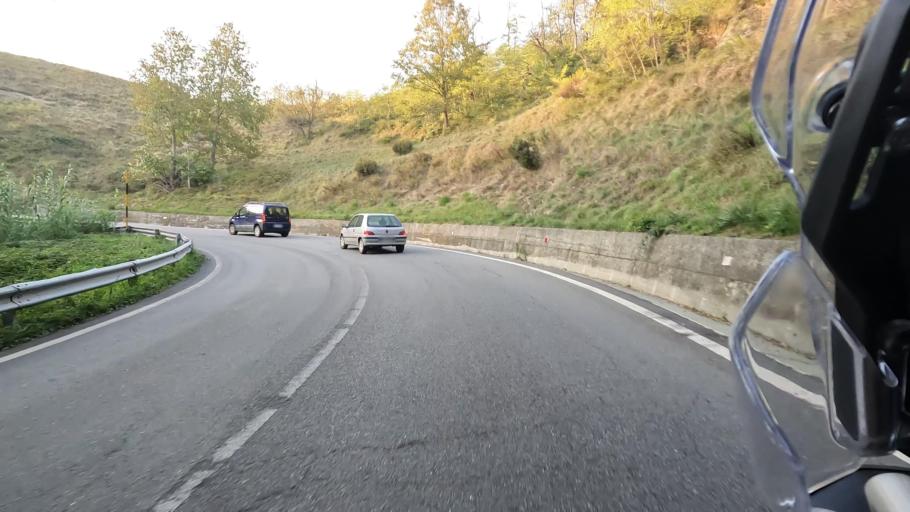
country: IT
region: Liguria
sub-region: Provincia di Savona
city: Osteria dei Cacciatori-Stella
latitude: 44.4228
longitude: 8.4753
